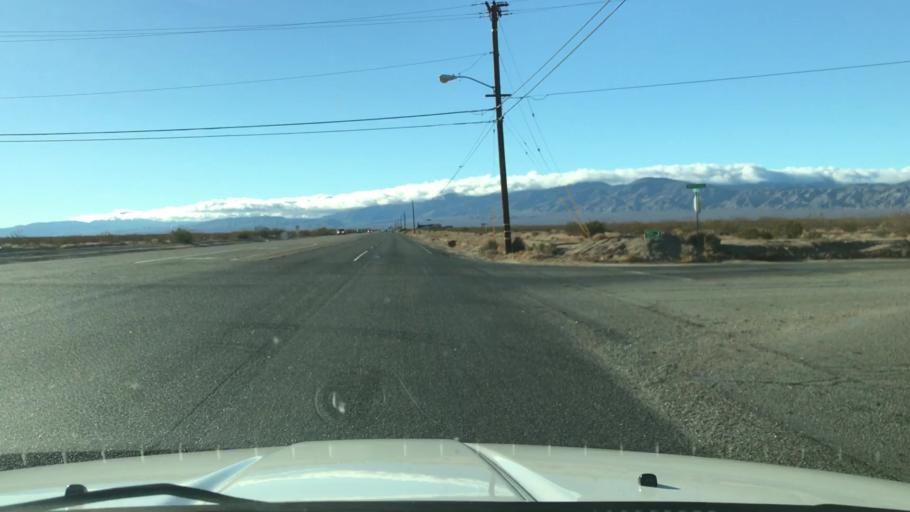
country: US
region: California
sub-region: Kern County
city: California City
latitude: 35.1248
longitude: -118.0136
